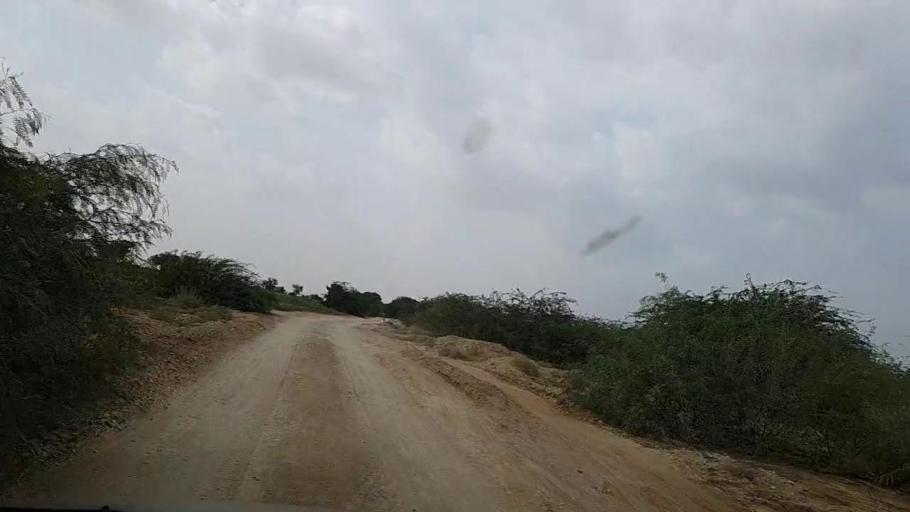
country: PK
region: Sindh
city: Kotri
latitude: 25.2781
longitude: 68.2560
